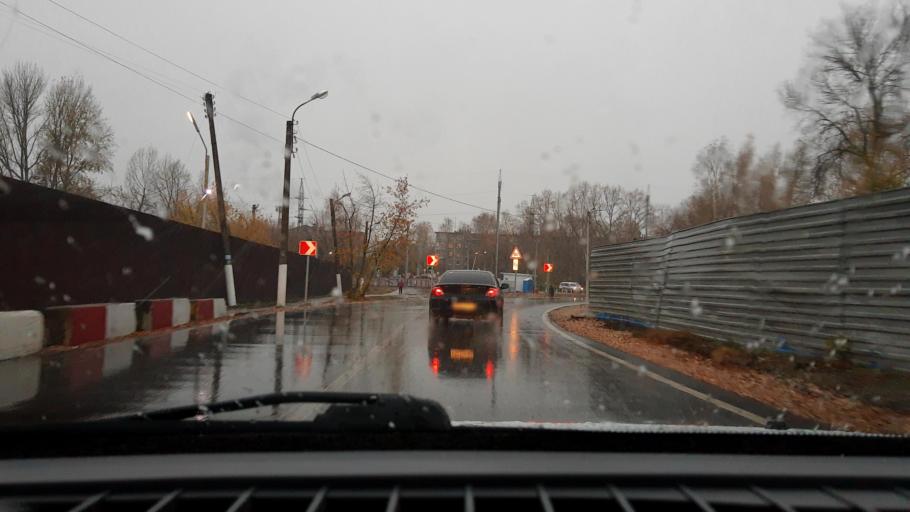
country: RU
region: Nizjnij Novgorod
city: Gorbatovka
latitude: 56.3505
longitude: 43.8411
